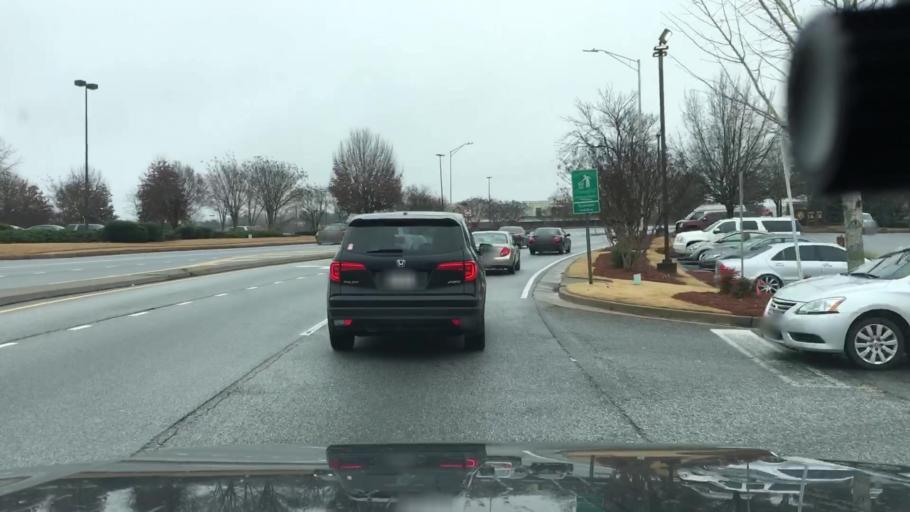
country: US
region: Georgia
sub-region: Coweta County
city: Newnan
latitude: 33.3947
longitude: -84.7614
